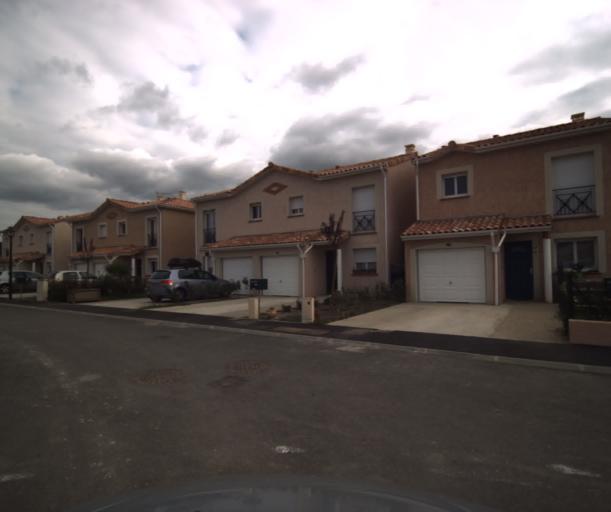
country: FR
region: Midi-Pyrenees
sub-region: Departement de la Haute-Garonne
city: Muret
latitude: 43.4448
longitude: 1.3211
